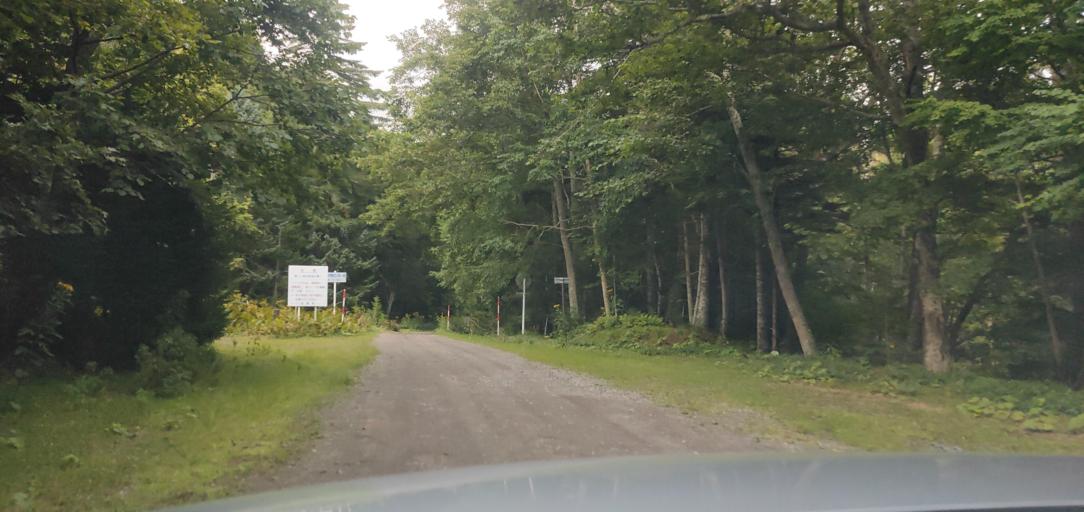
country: JP
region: Hokkaido
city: Kitami
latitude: 43.3702
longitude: 143.9454
